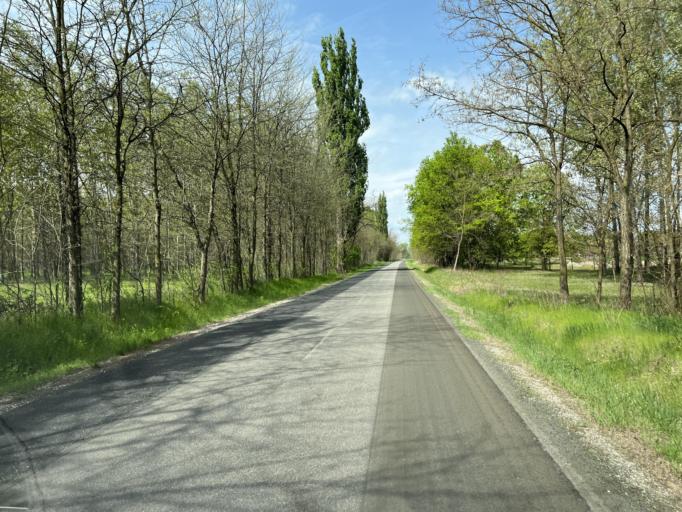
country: HU
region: Pest
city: Albertirsa
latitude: 47.1927
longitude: 19.6121
